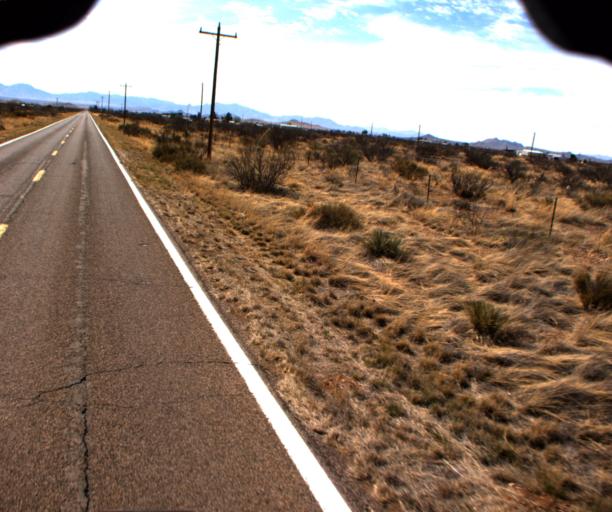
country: US
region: Arizona
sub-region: Cochise County
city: Willcox
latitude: 31.8762
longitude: -109.6047
